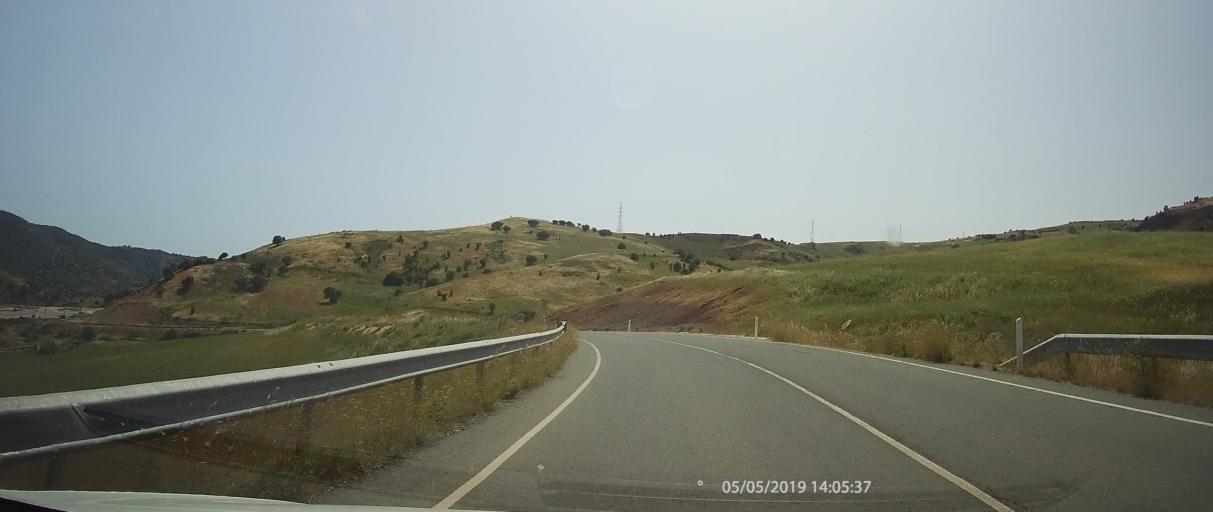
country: CY
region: Limassol
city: Pissouri
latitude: 34.7516
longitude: 32.6111
